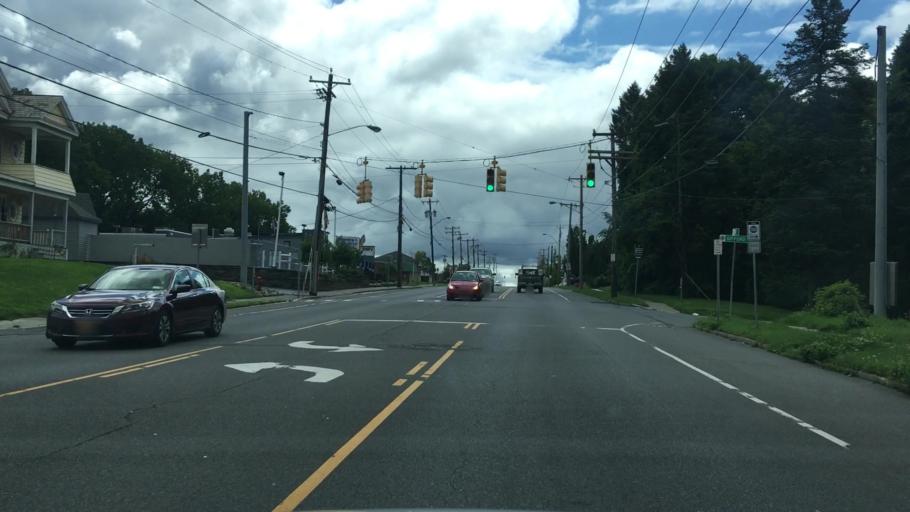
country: US
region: New York
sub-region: Schenectady County
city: Niskayuna
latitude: 42.7761
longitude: -73.8993
